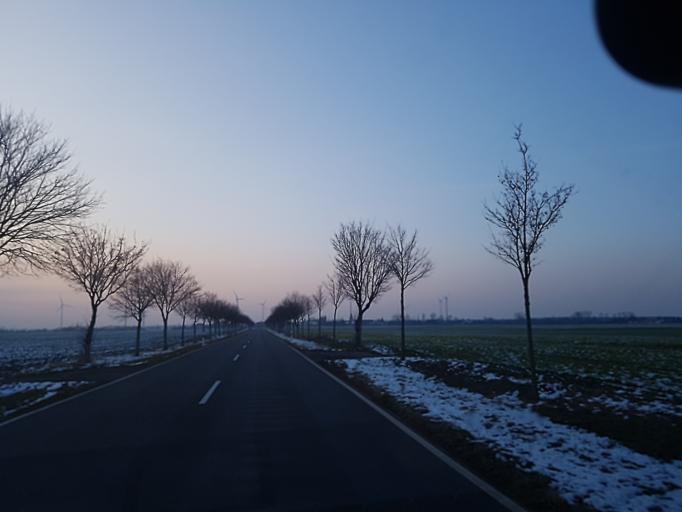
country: DE
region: Brandenburg
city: Muhlberg
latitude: 51.4704
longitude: 13.2821
